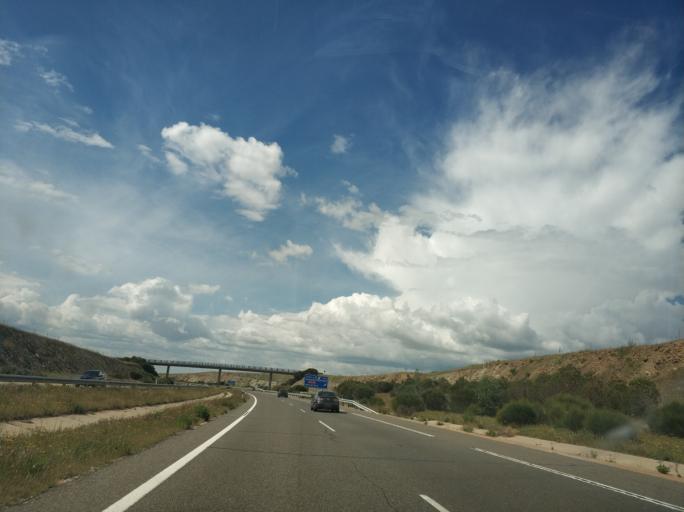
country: ES
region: Castille and Leon
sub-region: Provincia de Salamanca
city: Mozarbez
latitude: 40.8583
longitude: -5.6415
